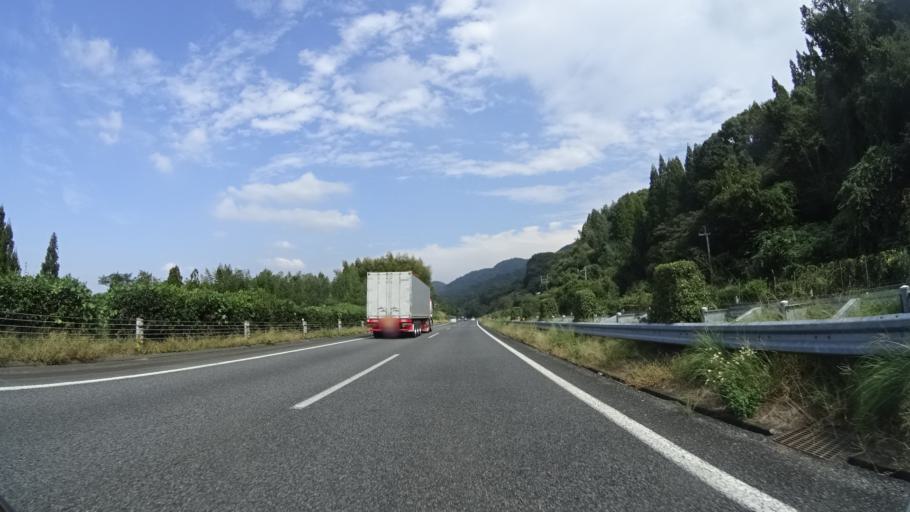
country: JP
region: Kumamoto
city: Matsubase
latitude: 32.5957
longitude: 130.7175
